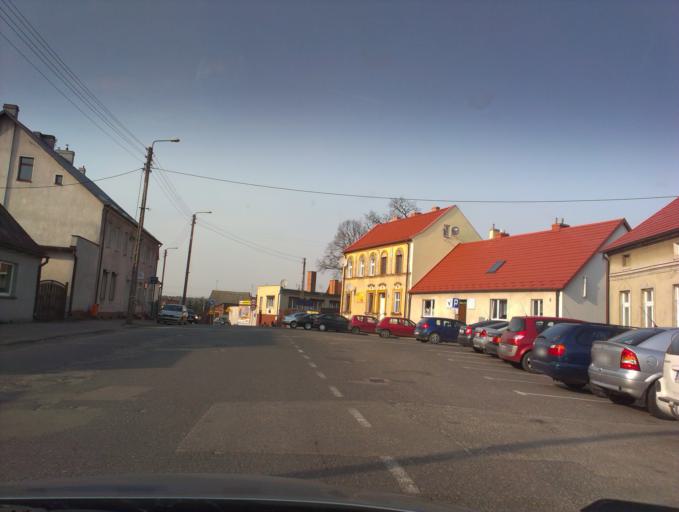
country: PL
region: Kujawsko-Pomorskie
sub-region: Powiat sepolenski
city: Sepolno Krajenskie
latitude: 53.4497
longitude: 17.5286
